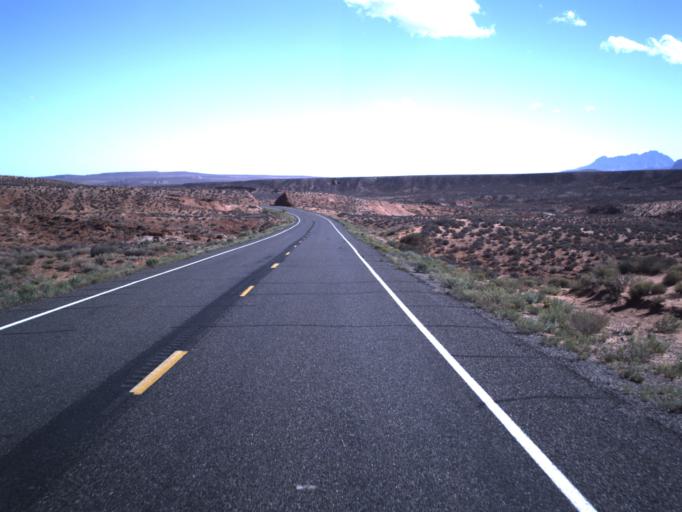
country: US
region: Utah
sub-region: Wayne County
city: Loa
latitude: 38.0728
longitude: -110.6080
